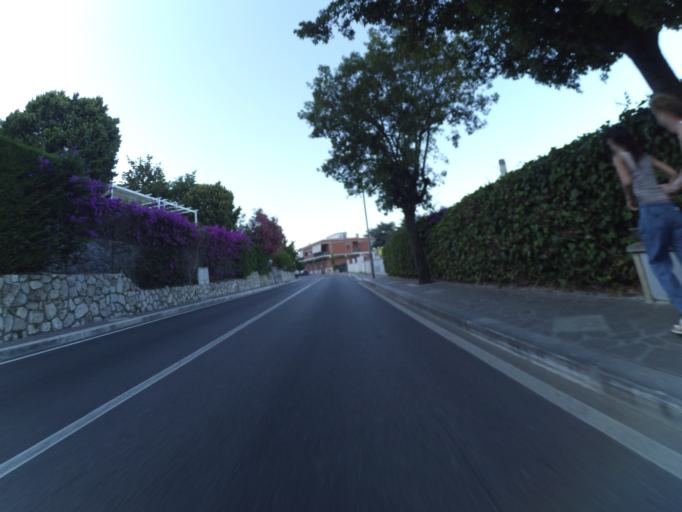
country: IT
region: Latium
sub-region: Provincia di Latina
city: San Felice Circeo
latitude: 41.2400
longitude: 13.0917
